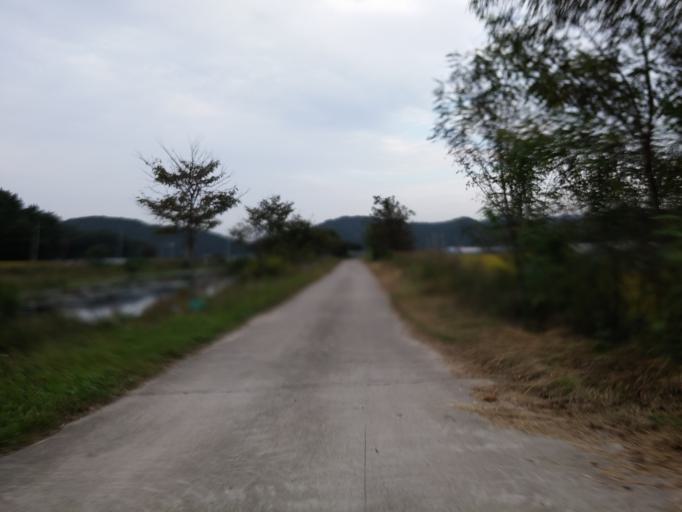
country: KR
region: Daejeon
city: Daejeon
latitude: 36.2444
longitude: 127.3115
